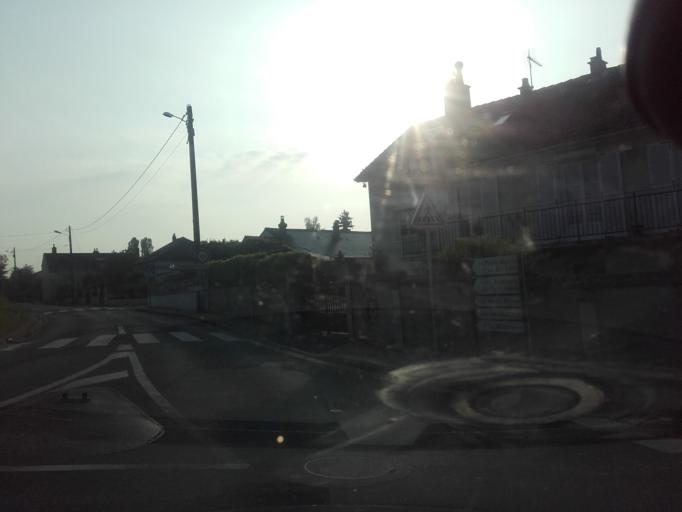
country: FR
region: Centre
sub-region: Departement d'Indre-et-Loire
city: Parcay-Meslay
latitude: 47.4428
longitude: 0.7491
